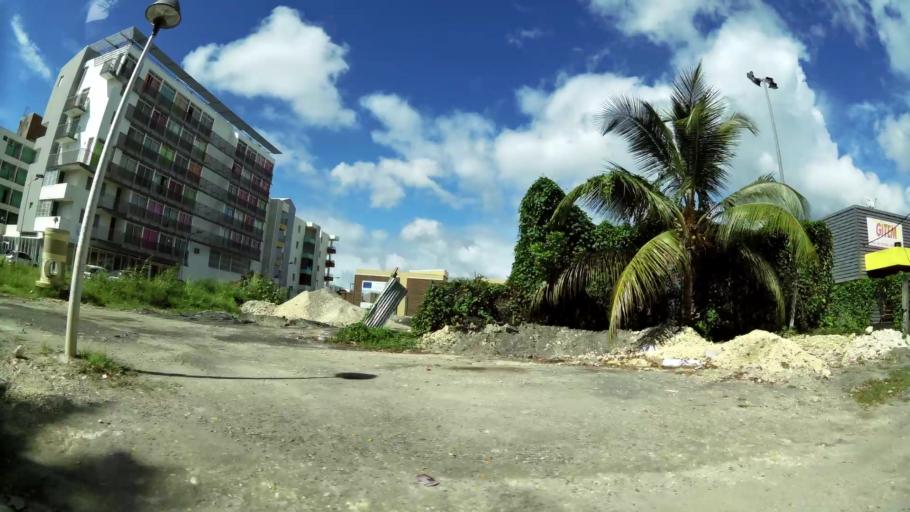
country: GP
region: Guadeloupe
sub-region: Guadeloupe
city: Pointe-a-Pitre
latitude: 16.2455
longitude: -61.5389
